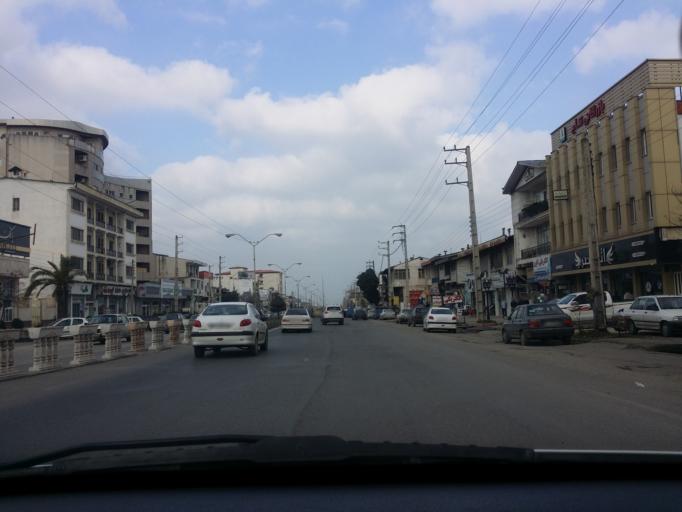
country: IR
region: Mazandaran
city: Chalus
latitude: 36.6667
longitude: 51.4099
